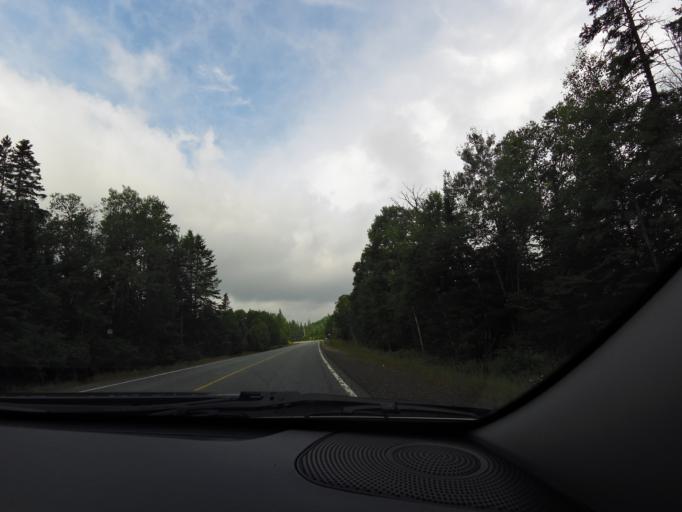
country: CA
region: Ontario
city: Huntsville
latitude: 45.5427
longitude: -79.2648
